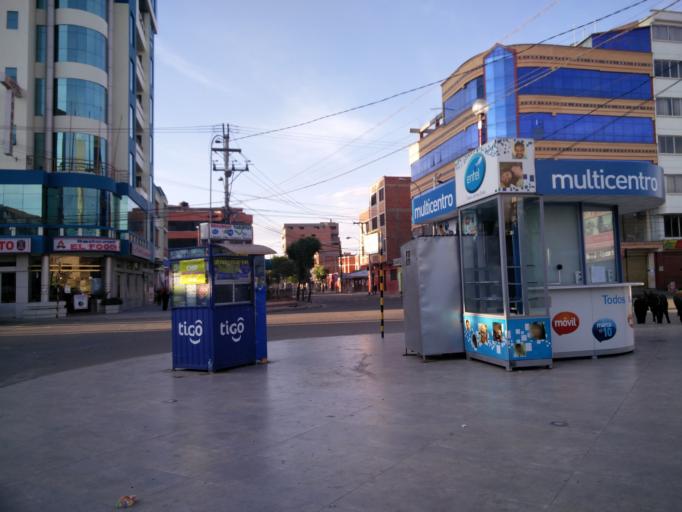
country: BO
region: Oruro
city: Oruro
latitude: -17.9622
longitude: -67.1039
